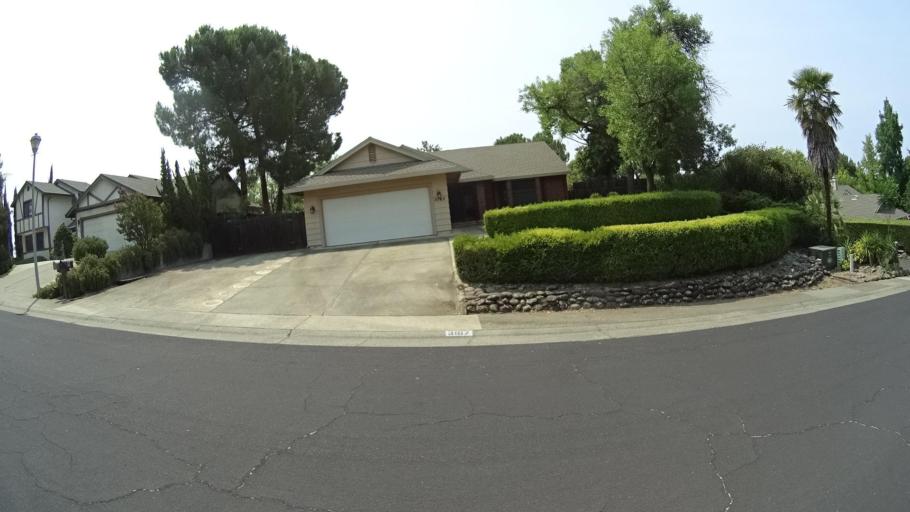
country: US
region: California
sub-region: Placer County
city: Rocklin
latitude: 38.8045
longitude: -121.2507
